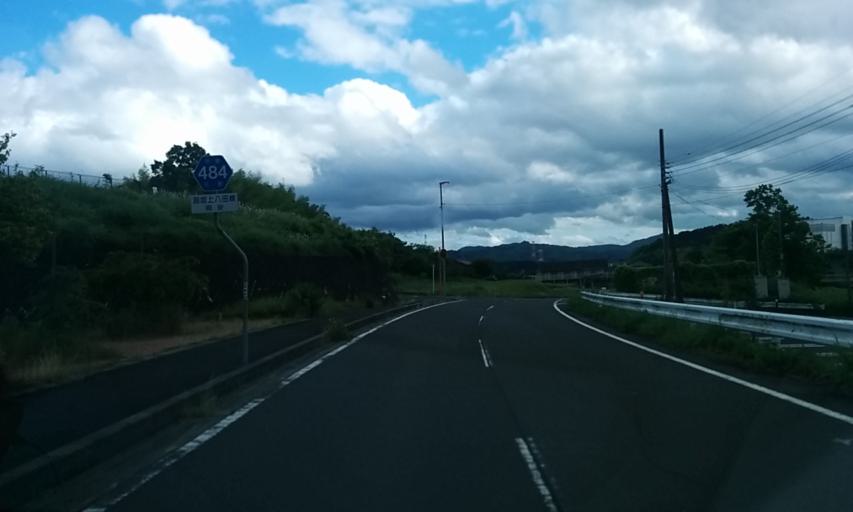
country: JP
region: Kyoto
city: Ayabe
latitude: 35.3363
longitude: 135.2938
